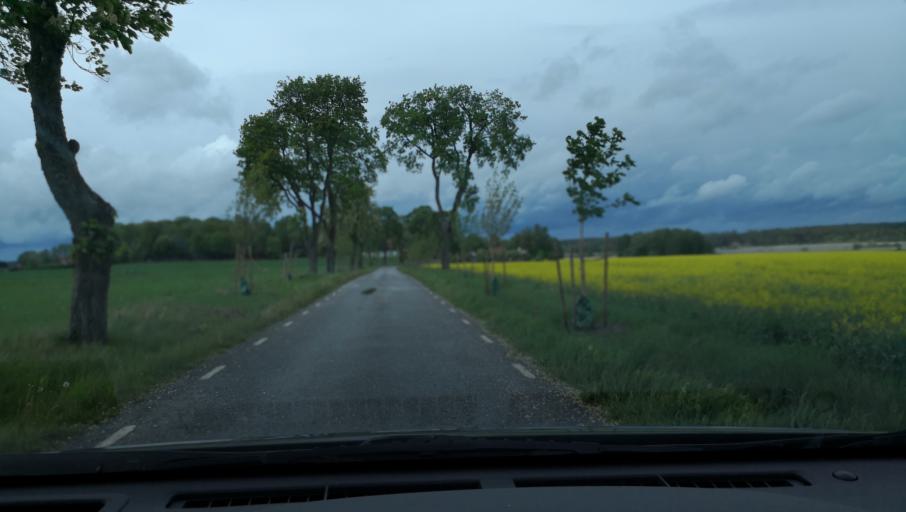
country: SE
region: Uppsala
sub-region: Enkopings Kommun
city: Orsundsbro
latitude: 59.7217
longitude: 17.4198
